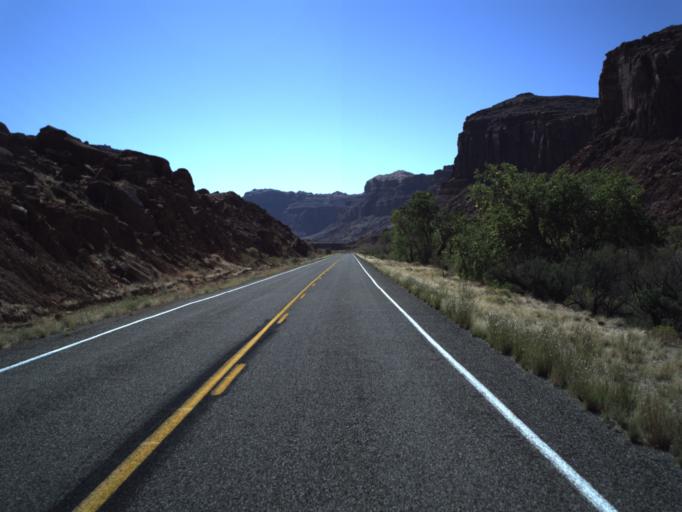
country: US
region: Utah
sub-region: San Juan County
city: Blanding
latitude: 37.9430
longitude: -110.4702
